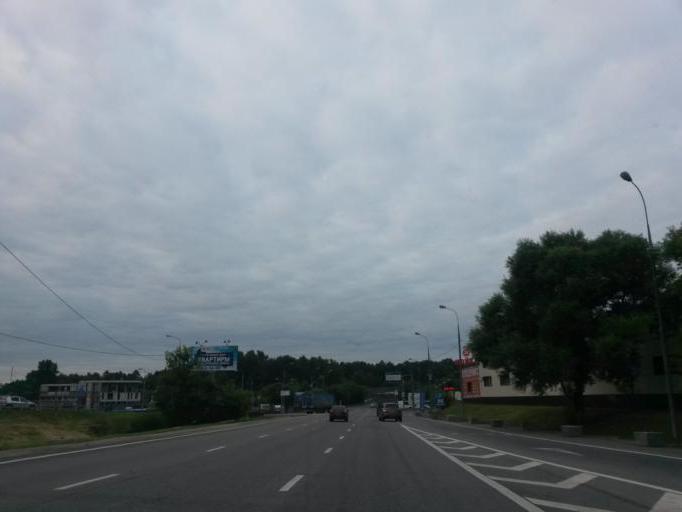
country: RU
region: Moscow
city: Annino
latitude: 55.5690
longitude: 37.5975
